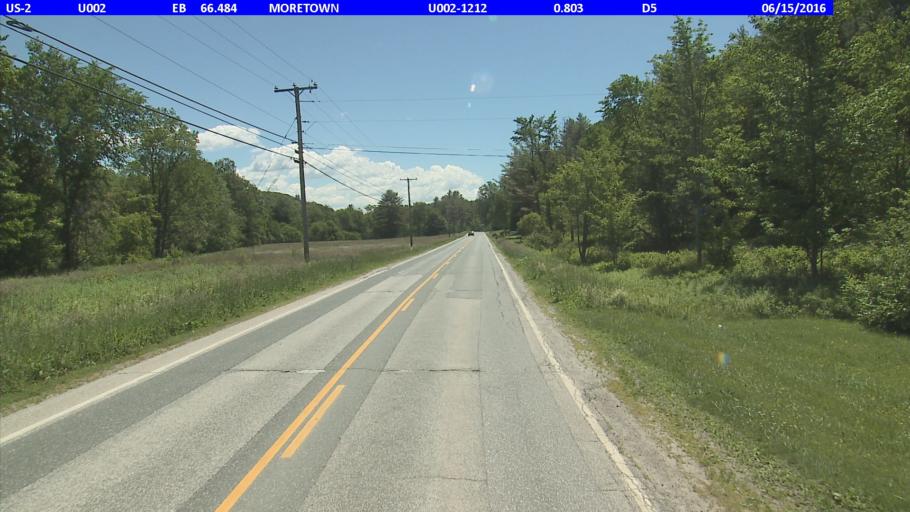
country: US
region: Vermont
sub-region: Washington County
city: Waterbury
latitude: 44.3206
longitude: -72.7337
